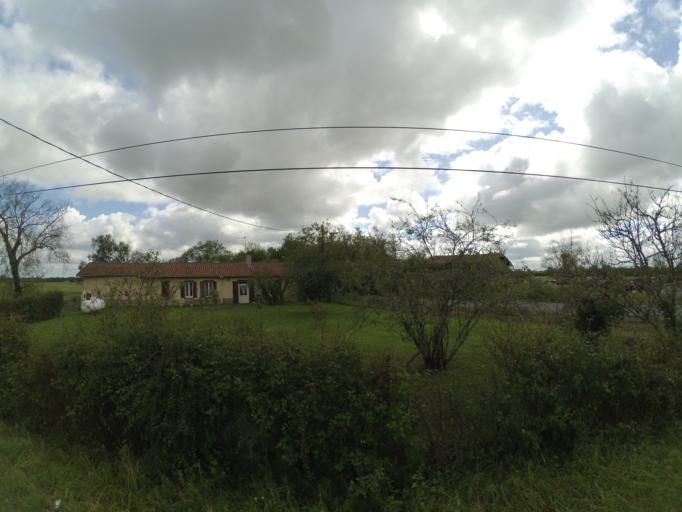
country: FR
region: Aquitaine
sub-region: Departement de la Gironde
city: Ludon-Medoc
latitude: 44.9973
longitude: -0.5932
